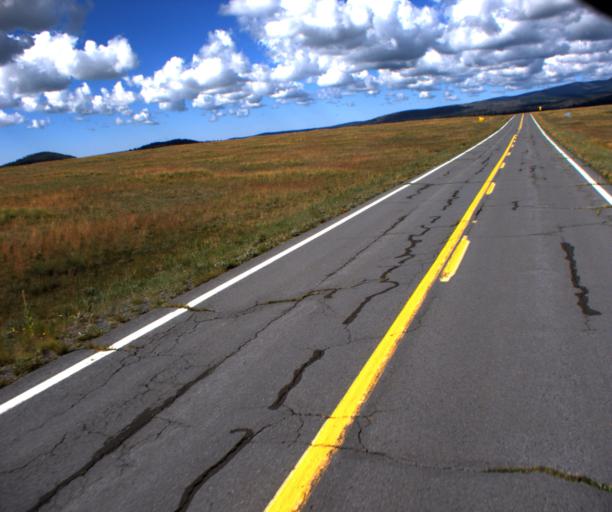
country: US
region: Arizona
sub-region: Apache County
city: Eagar
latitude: 33.9626
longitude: -109.3888
